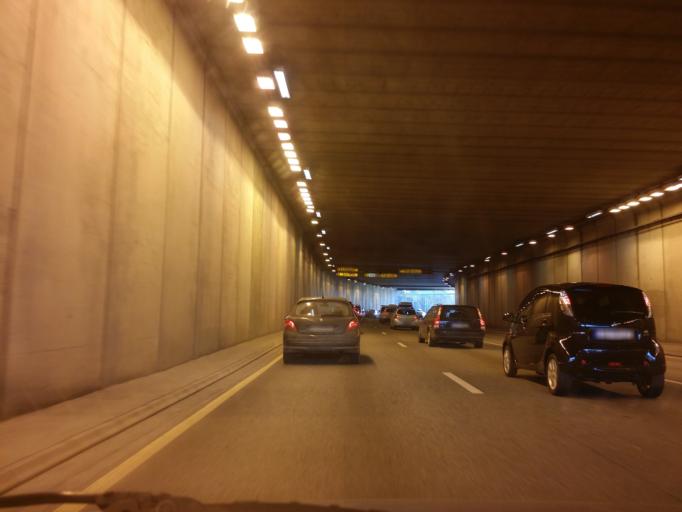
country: NO
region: Akershus
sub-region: Baerum
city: Lysaker
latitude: 59.9086
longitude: 10.6277
